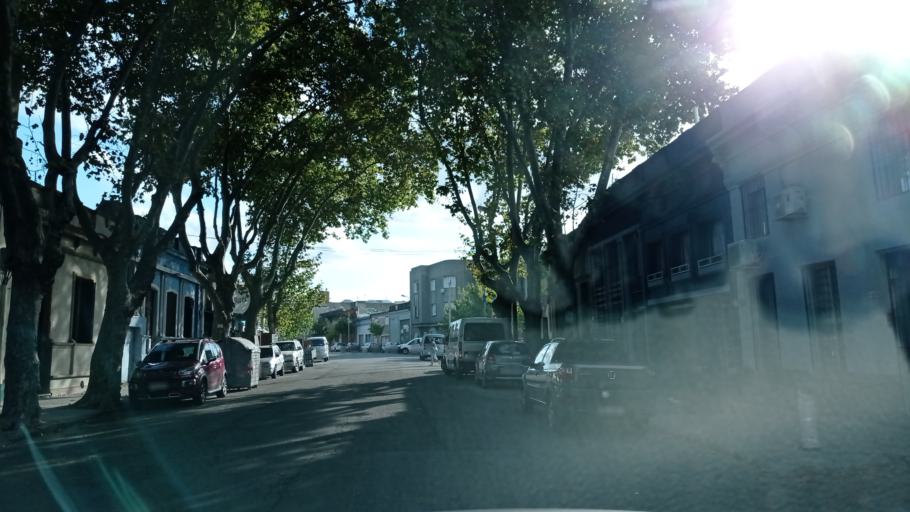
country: UY
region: Montevideo
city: Montevideo
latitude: -34.8929
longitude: -56.1802
